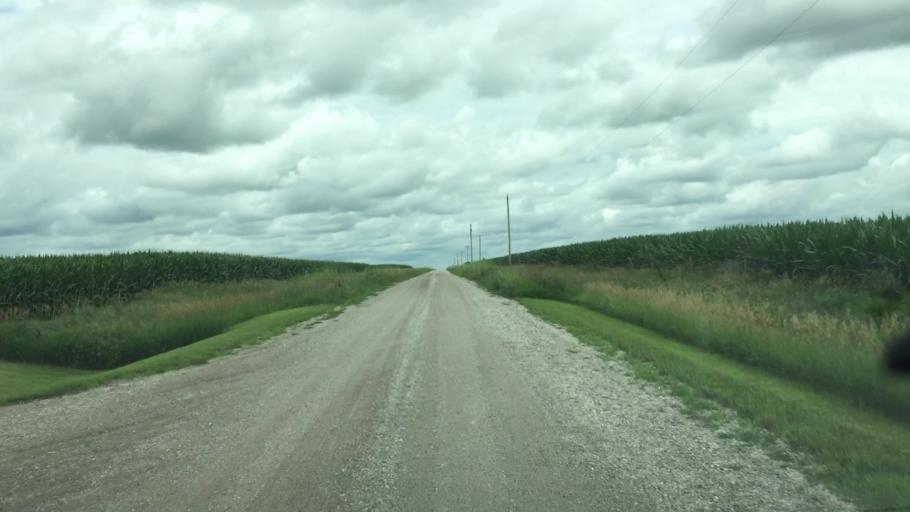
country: US
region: Iowa
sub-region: Jasper County
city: Monroe
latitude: 41.5701
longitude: -93.1208
